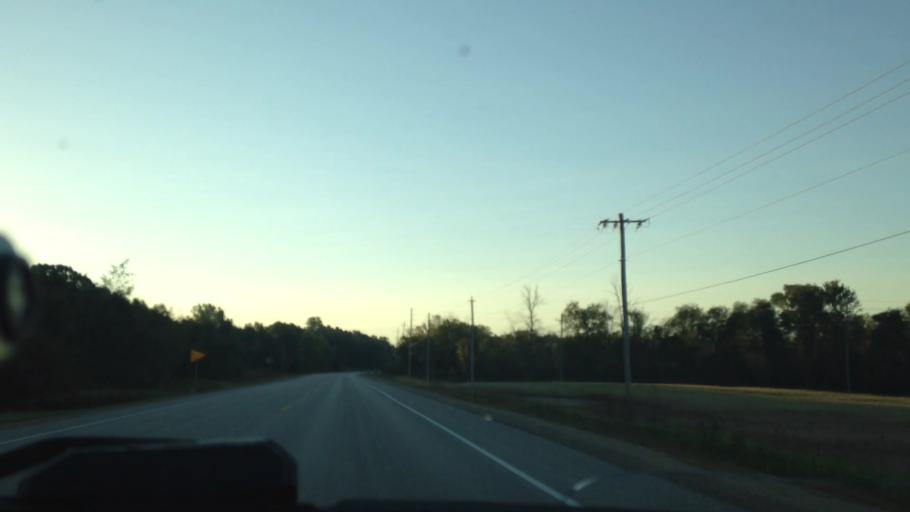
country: US
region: Wisconsin
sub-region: Washington County
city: Newburg
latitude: 43.4265
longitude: -88.0359
